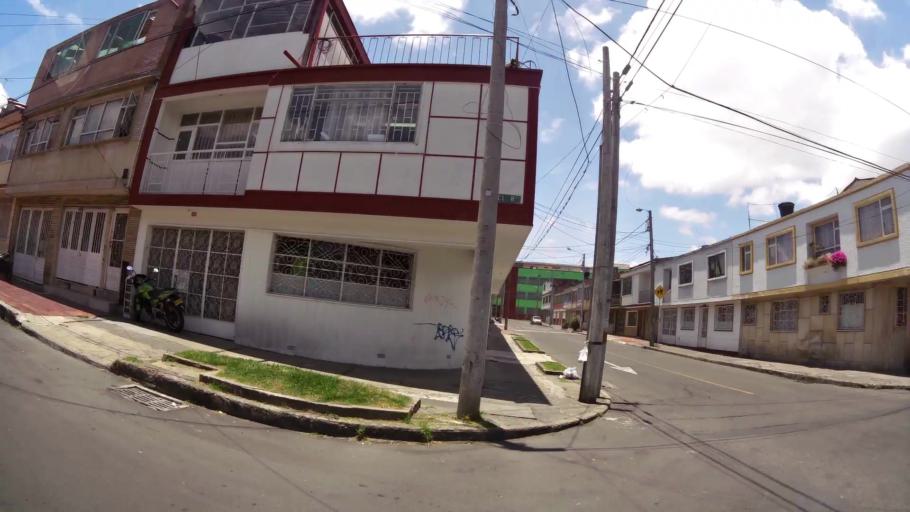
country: CO
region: Bogota D.C.
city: Bogota
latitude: 4.5889
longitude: -74.0950
